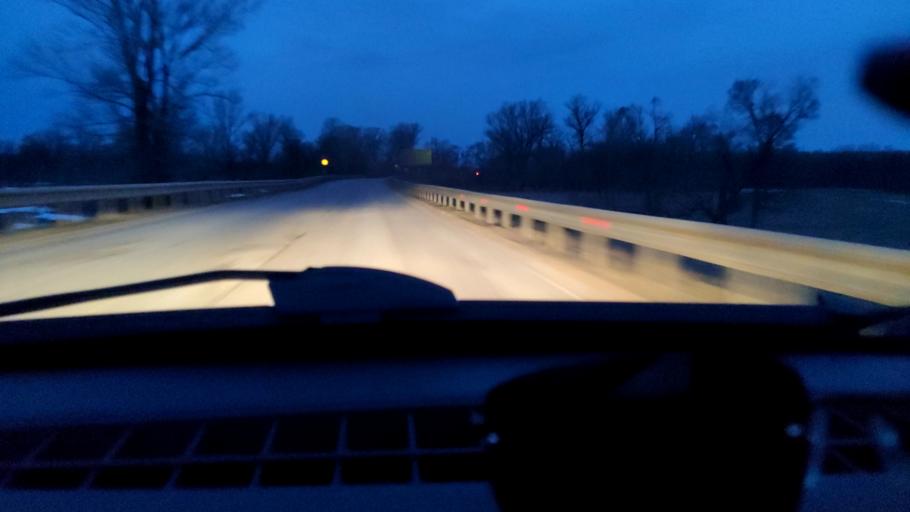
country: RU
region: Bashkortostan
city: Kabakovo
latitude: 54.5670
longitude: 55.9843
